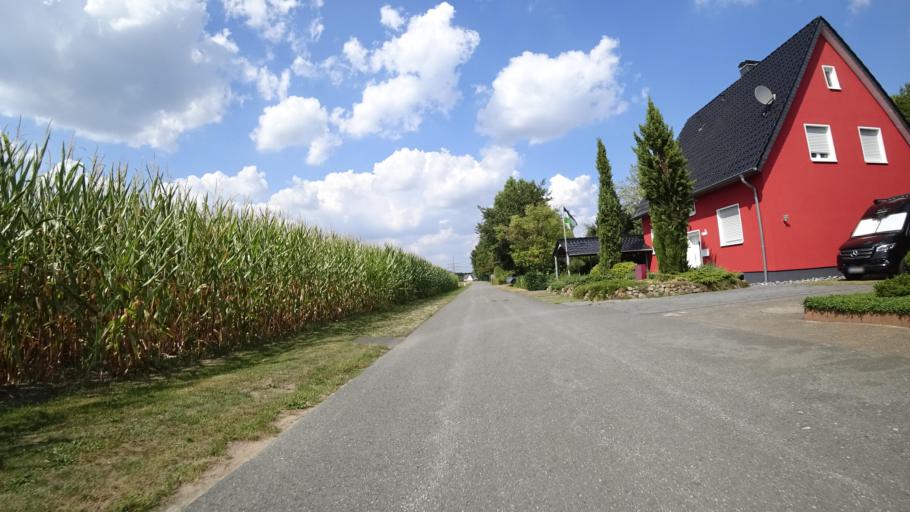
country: DE
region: North Rhine-Westphalia
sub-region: Regierungsbezirk Detmold
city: Guetersloh
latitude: 51.9215
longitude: 8.4237
